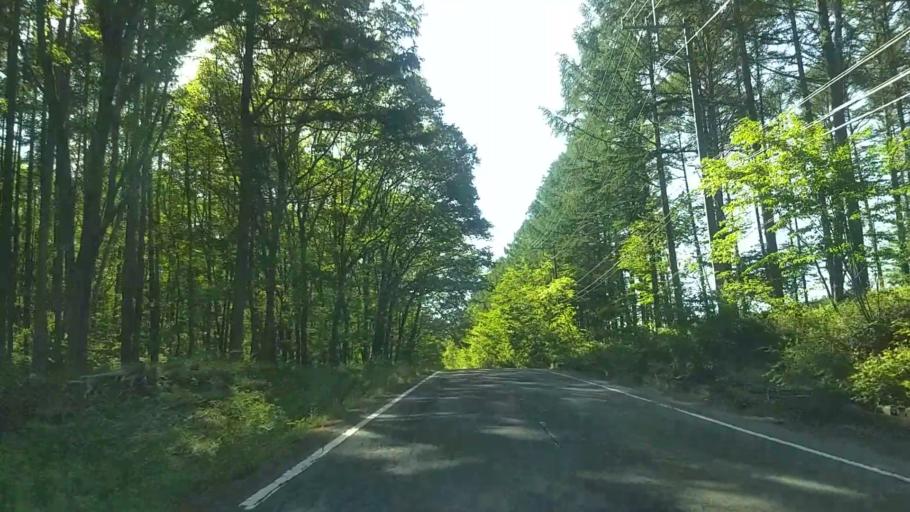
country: JP
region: Yamanashi
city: Nirasaki
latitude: 35.8892
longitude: 138.3558
